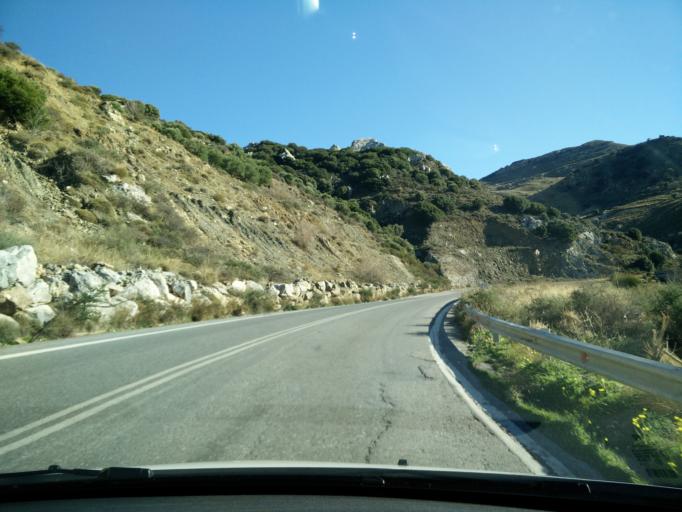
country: GR
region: Crete
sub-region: Nomos Irakleiou
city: Arkalochori
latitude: 35.0704
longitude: 25.3607
